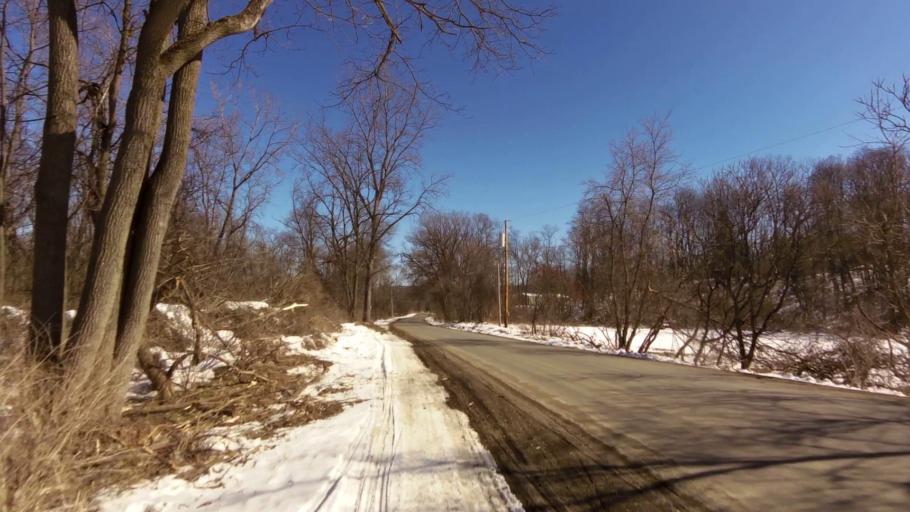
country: US
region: New York
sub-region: Allegany County
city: Houghton
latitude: 42.3629
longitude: -78.1399
